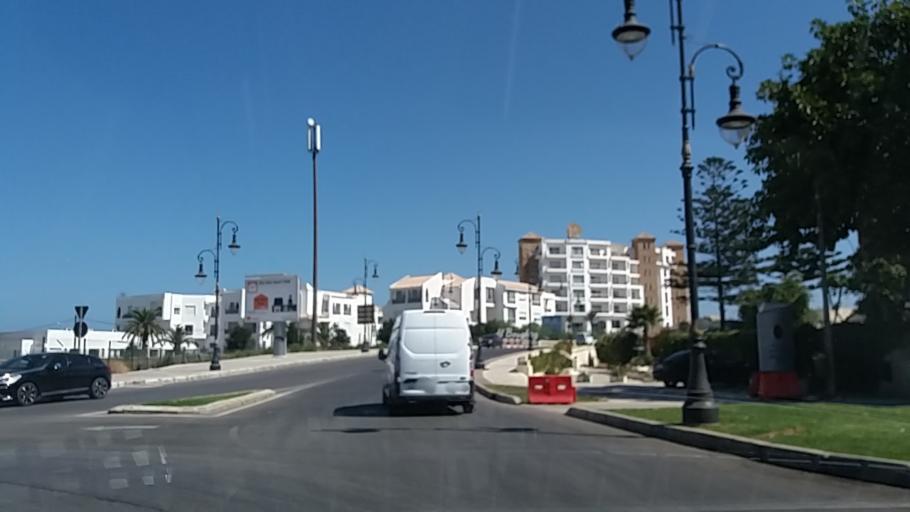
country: MA
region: Tanger-Tetouan
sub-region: Tanger-Assilah
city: Tangier
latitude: 35.7850
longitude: -5.7615
